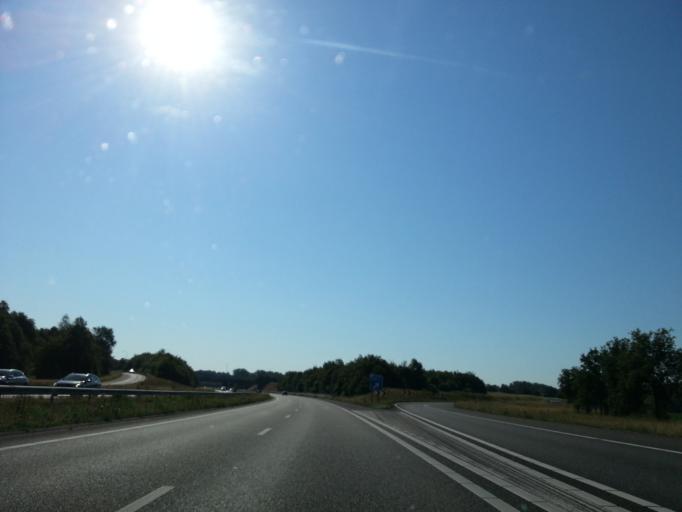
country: NL
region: Limburg
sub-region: Gemeente Weert
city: Weert
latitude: 51.2780
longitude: 5.6589
